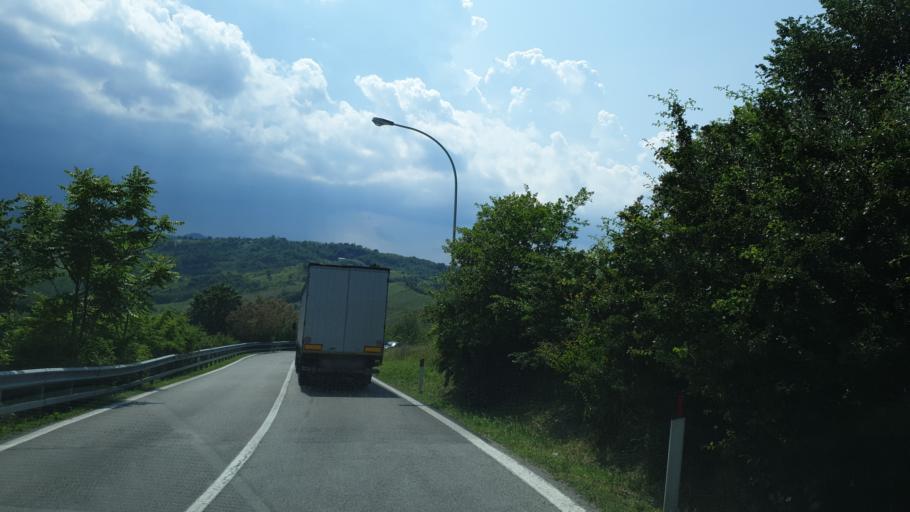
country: SM
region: Acquaviva
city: Acquaviva
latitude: 43.9483
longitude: 12.4125
